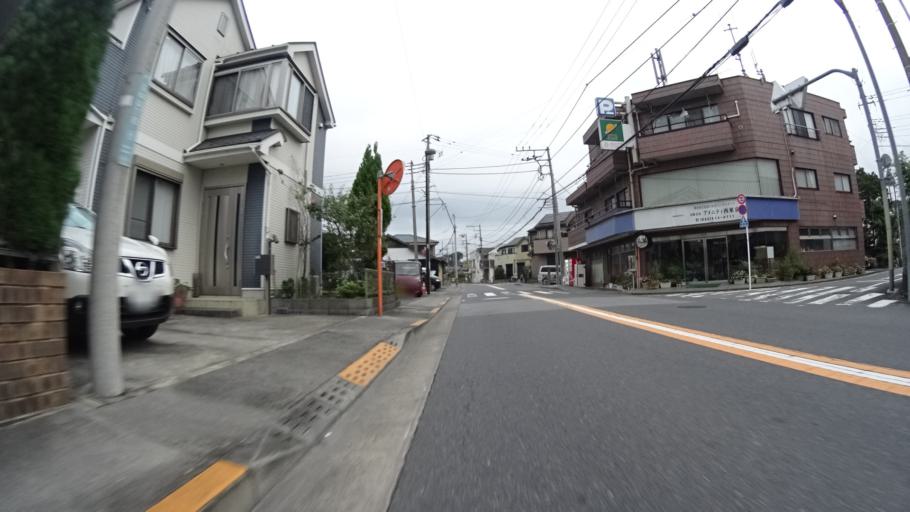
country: JP
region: Tokyo
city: Fussa
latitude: 35.7580
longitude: 139.3075
